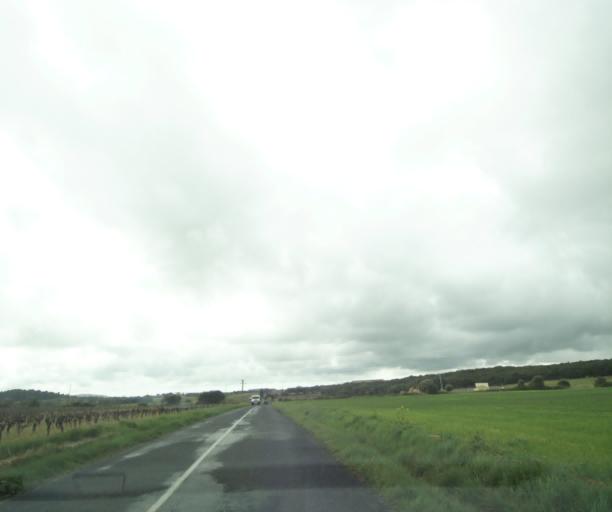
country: FR
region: Languedoc-Roussillon
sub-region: Departement de l'Herault
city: Cournonsec
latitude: 43.5376
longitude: 3.6985
